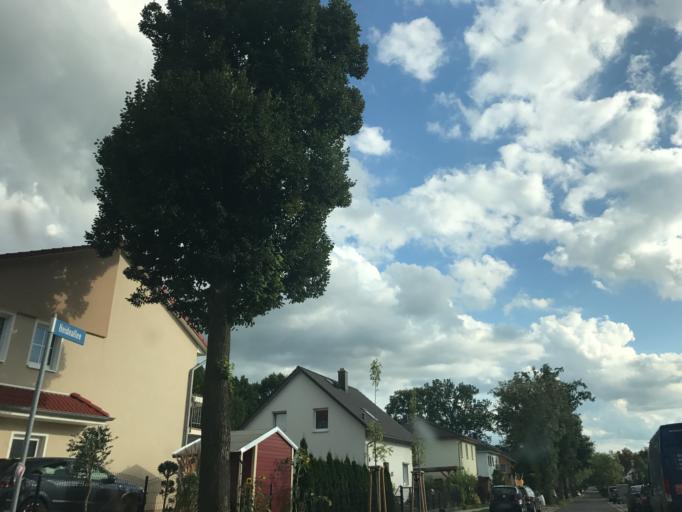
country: DE
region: Brandenburg
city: Dallgow-Doeberitz
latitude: 52.5406
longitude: 13.0524
